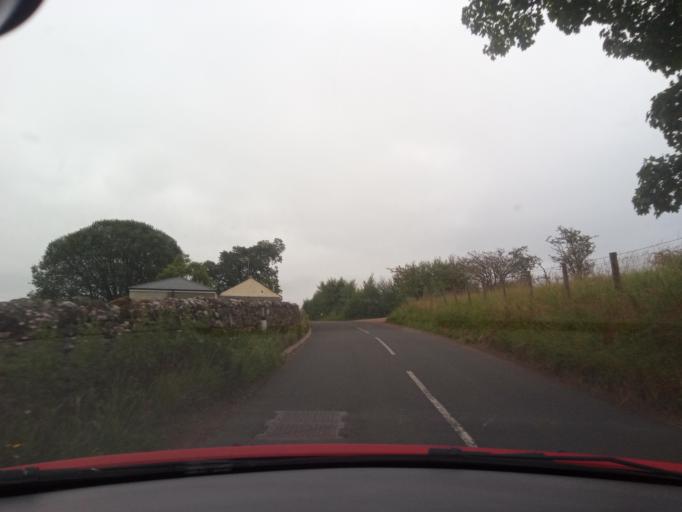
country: GB
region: England
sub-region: Northumberland
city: Otterburn
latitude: 55.3323
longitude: -2.0971
